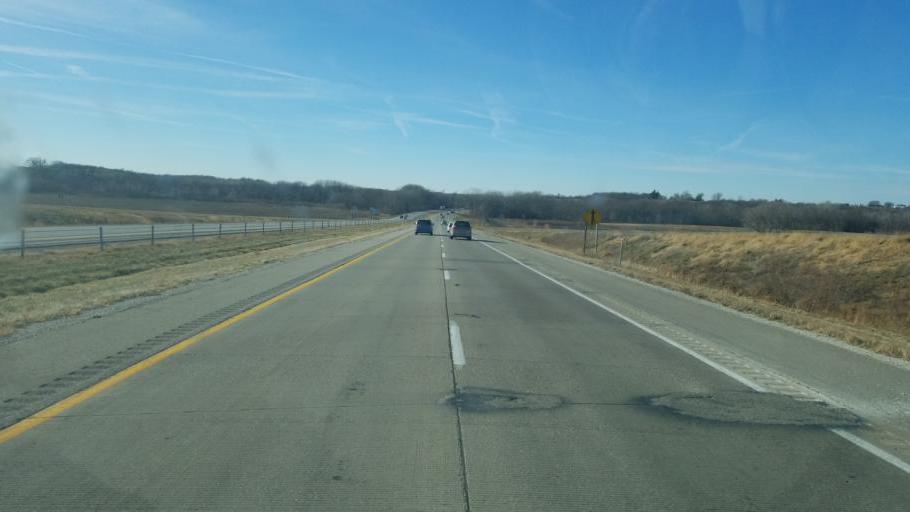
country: US
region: Iowa
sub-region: Dallas County
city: Van Meter
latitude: 41.5478
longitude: -93.9550
